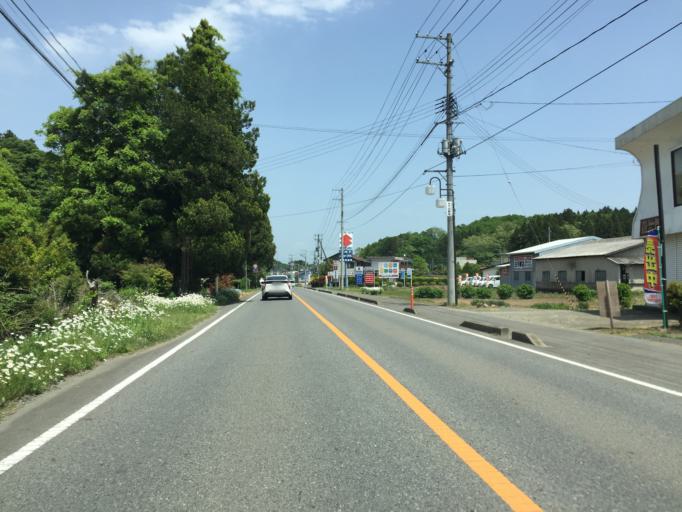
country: JP
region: Fukushima
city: Ishikawa
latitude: 37.1164
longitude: 140.3448
